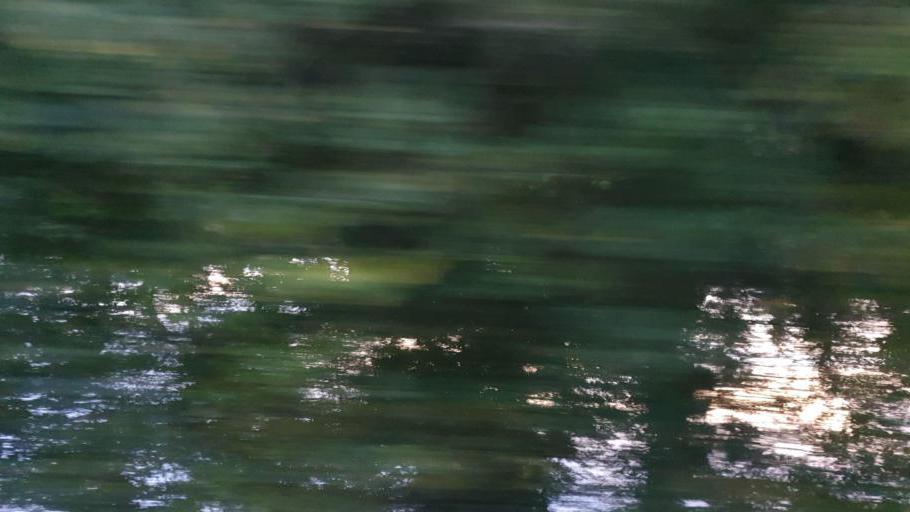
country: NO
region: Nord-Trondelag
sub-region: Levanger
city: Skogn
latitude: 63.6769
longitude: 11.1332
